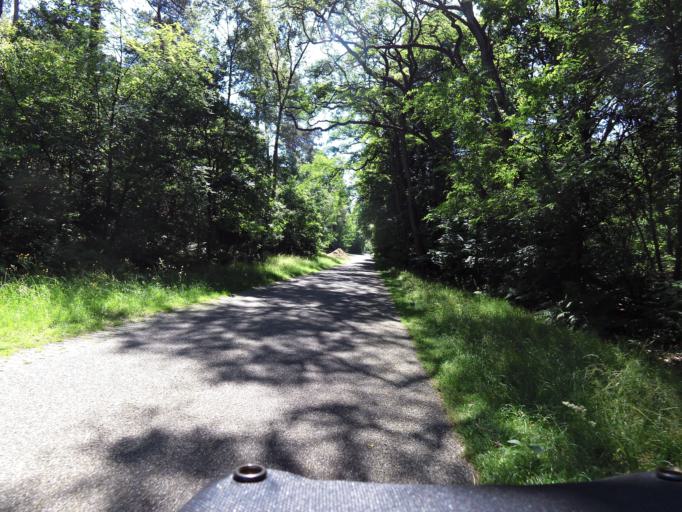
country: NL
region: Overijssel
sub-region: Gemeente Twenterand
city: Magele
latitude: 52.5103
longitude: 6.5337
